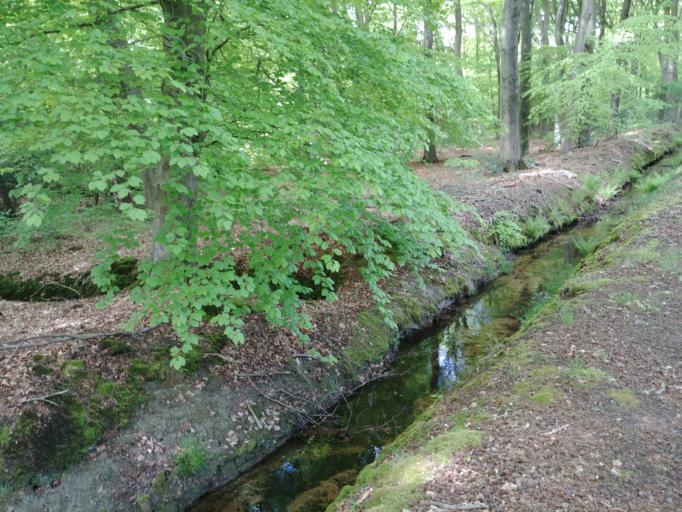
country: NL
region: Gelderland
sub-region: Gemeente Apeldoorn
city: Uddel
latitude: 52.2930
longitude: 5.7285
